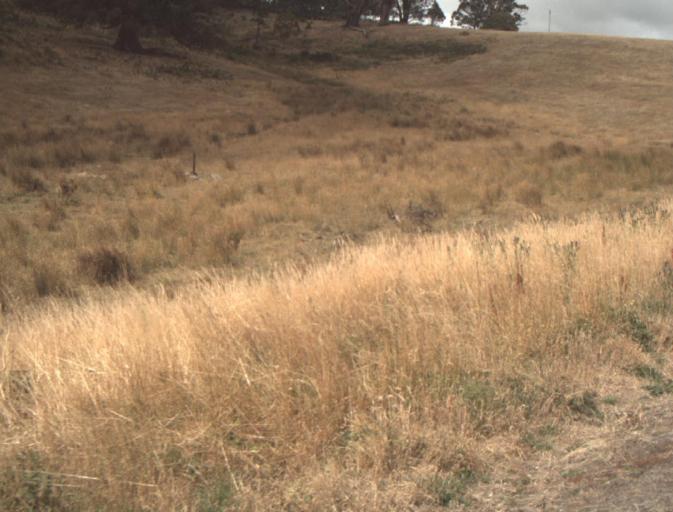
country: AU
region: Tasmania
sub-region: Northern Midlands
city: Evandale
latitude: -41.5194
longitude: 147.4693
